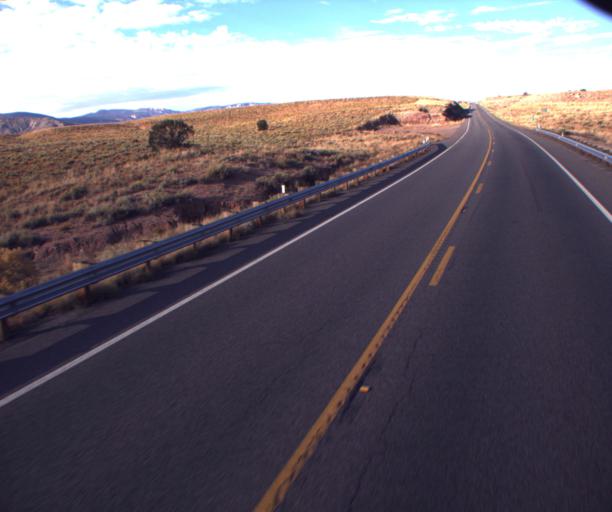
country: US
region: New Mexico
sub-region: San Juan County
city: Shiprock
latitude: 36.9362
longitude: -109.1232
